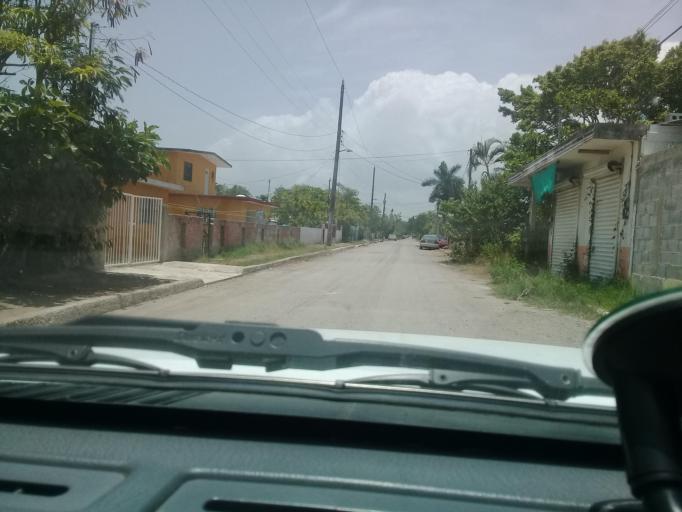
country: MX
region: Veracruz
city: Anahuac
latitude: 22.2251
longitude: -97.8182
